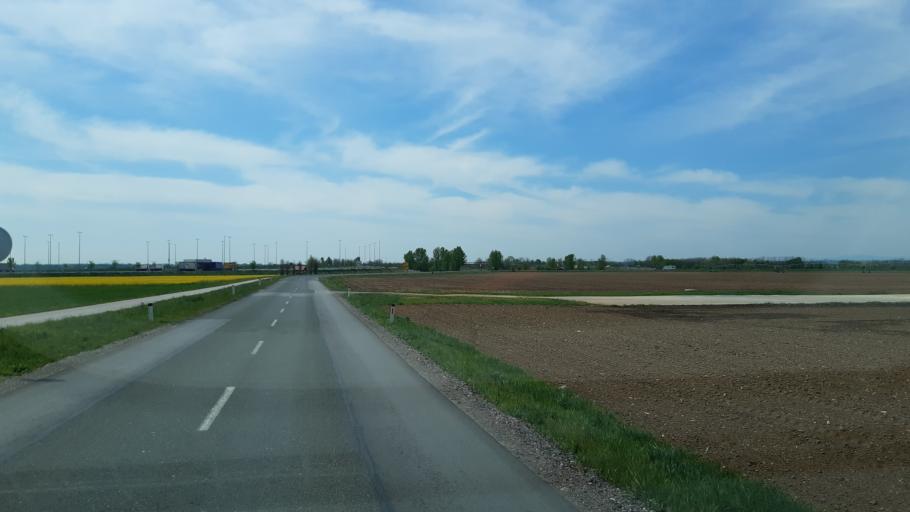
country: SI
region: Murska Sobota
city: Krog
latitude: 46.6388
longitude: 16.1639
